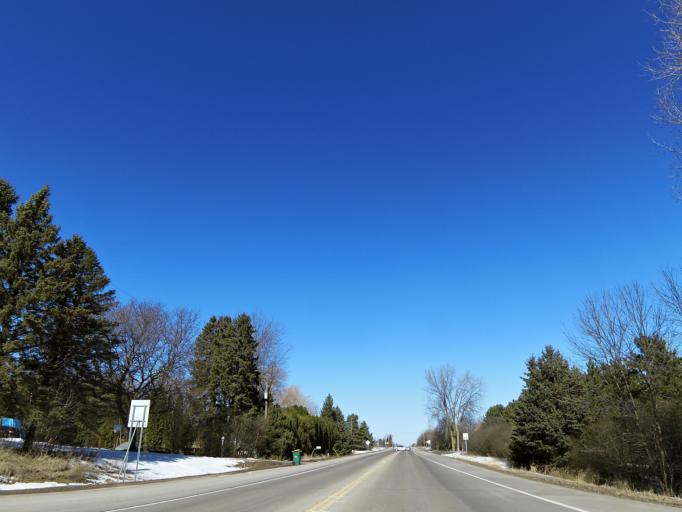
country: US
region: Minnesota
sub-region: Washington County
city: Lake Elmo
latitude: 45.0373
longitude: -92.8834
